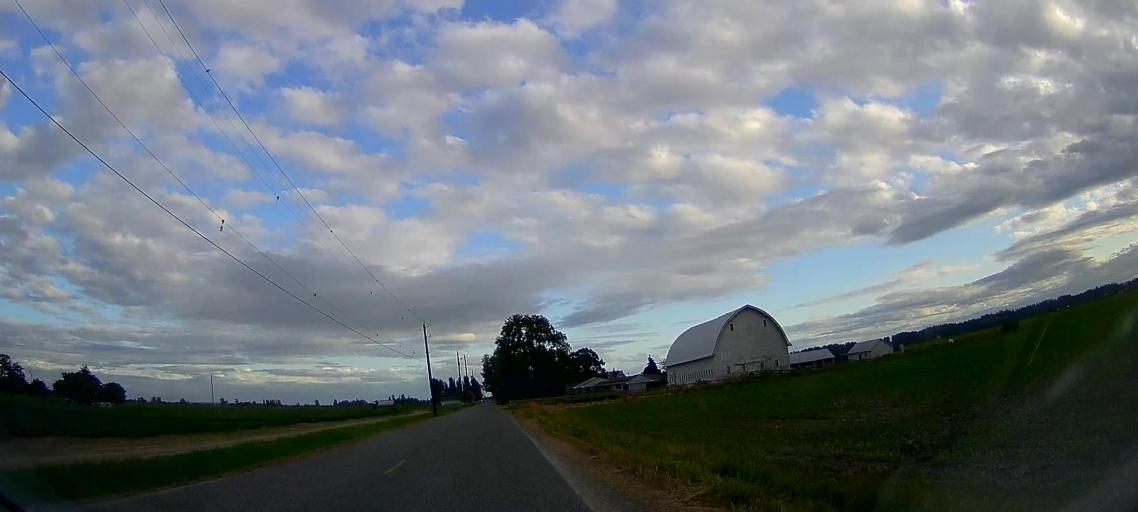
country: US
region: Washington
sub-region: Skagit County
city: Mount Vernon
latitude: 48.3827
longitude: -122.4001
